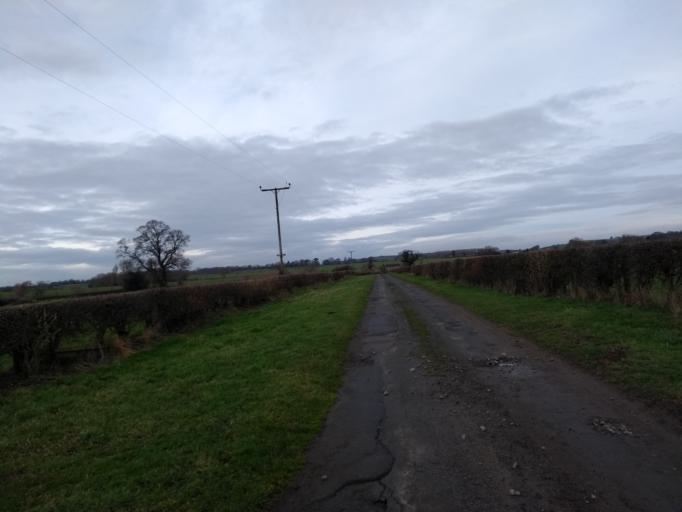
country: GB
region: England
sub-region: East Riding of Yorkshire
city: Stamford Bridge
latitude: 54.0663
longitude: -0.9320
